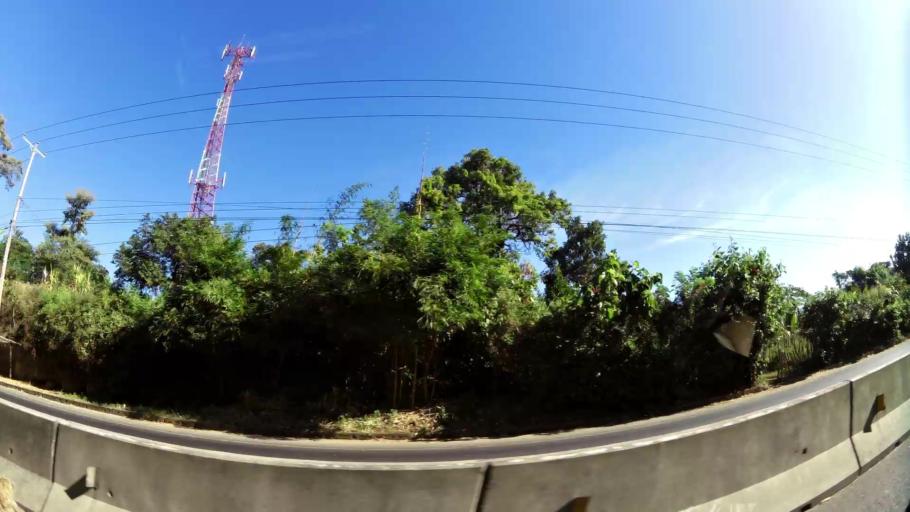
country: SV
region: Santa Ana
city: Coatepeque
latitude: 13.9403
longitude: -89.5443
